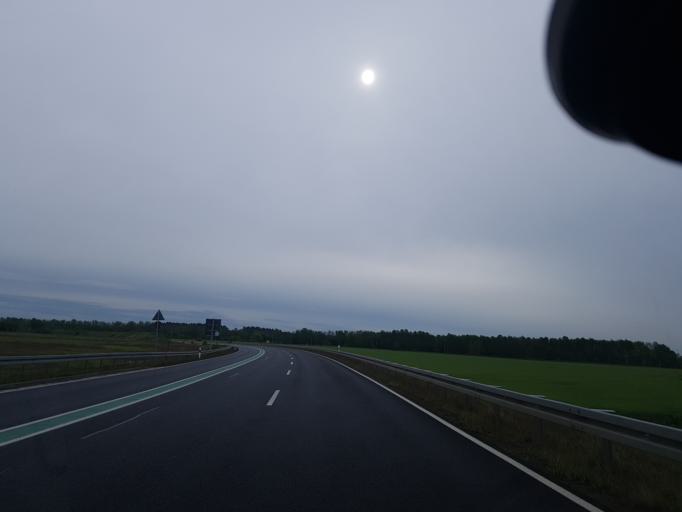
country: DE
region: Brandenburg
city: Neupetershain
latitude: 51.6325
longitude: 14.1860
